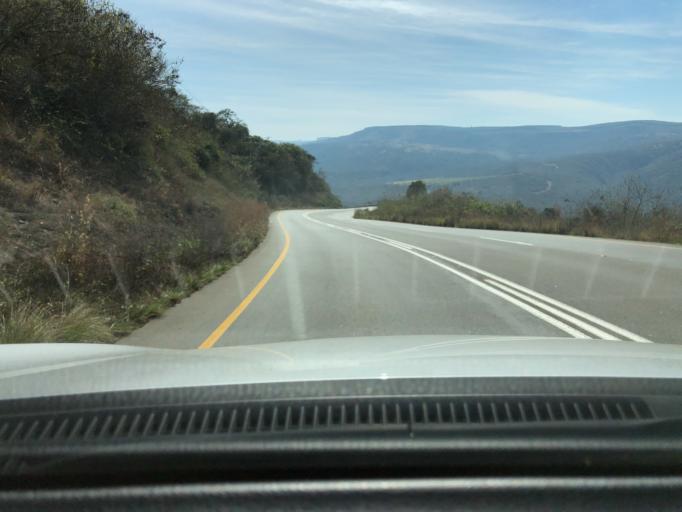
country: ZA
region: KwaZulu-Natal
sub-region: uMgungundlovu District Municipality
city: Richmond
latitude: -29.9893
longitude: 30.2469
